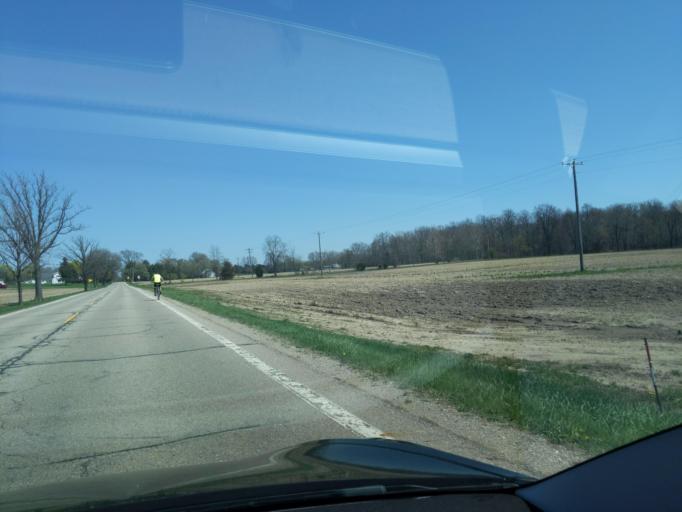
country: US
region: Michigan
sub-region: Ingham County
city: Stockbridge
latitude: 42.4538
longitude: -84.1578
